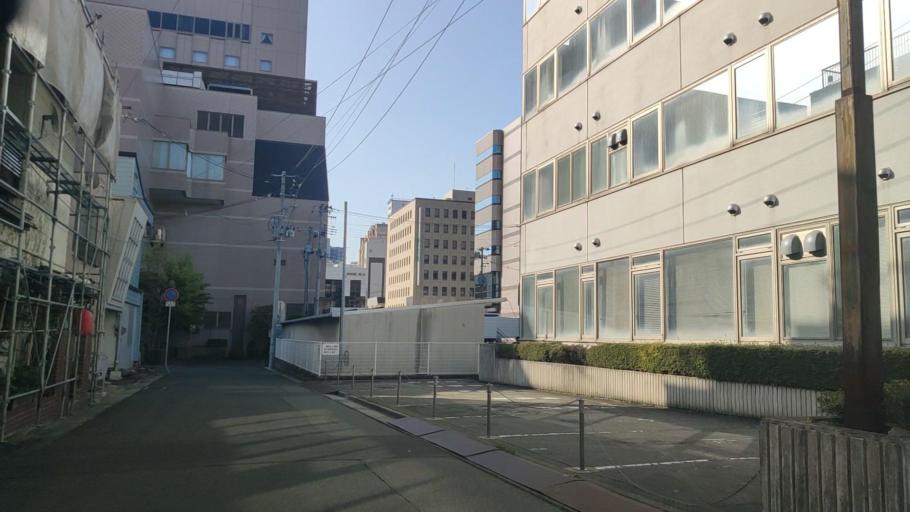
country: JP
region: Iwate
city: Morioka-shi
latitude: 39.7048
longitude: 141.1359
